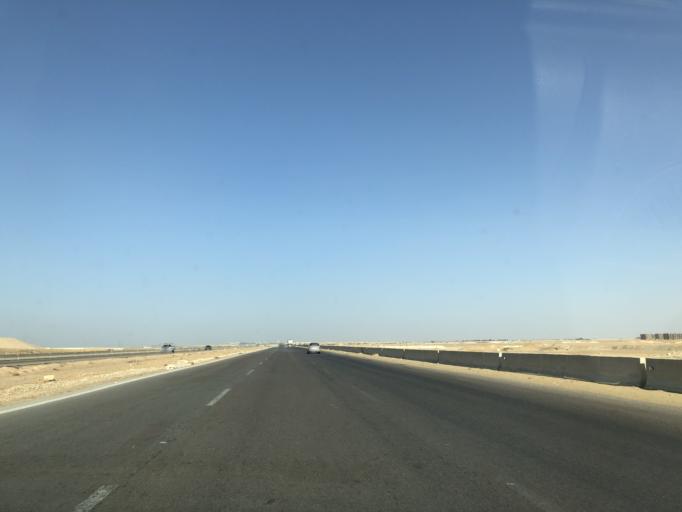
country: EG
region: Muhafazat al Minufiyah
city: Ashmun
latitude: 30.0676
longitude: 30.8827
